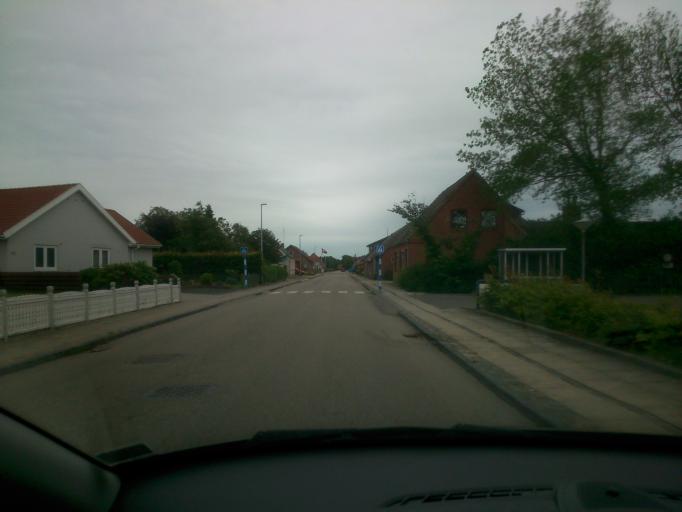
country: DK
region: Central Jutland
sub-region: Ringkobing-Skjern Kommune
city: Skjern
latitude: 55.9646
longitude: 8.3712
